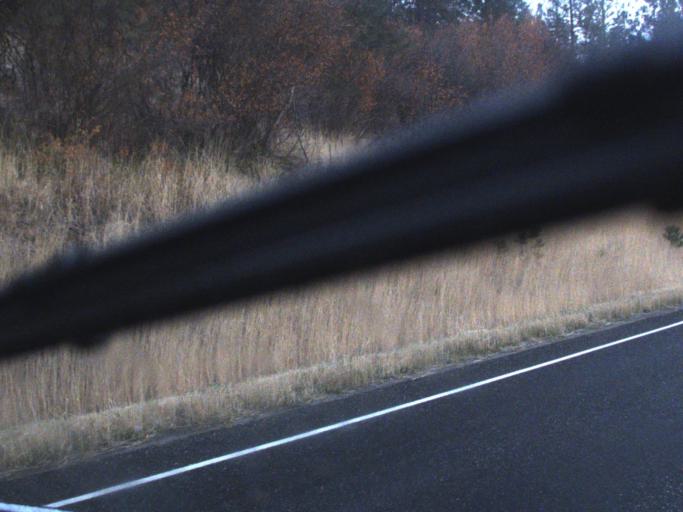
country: US
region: Washington
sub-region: Stevens County
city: Kettle Falls
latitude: 48.4570
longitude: -118.1790
